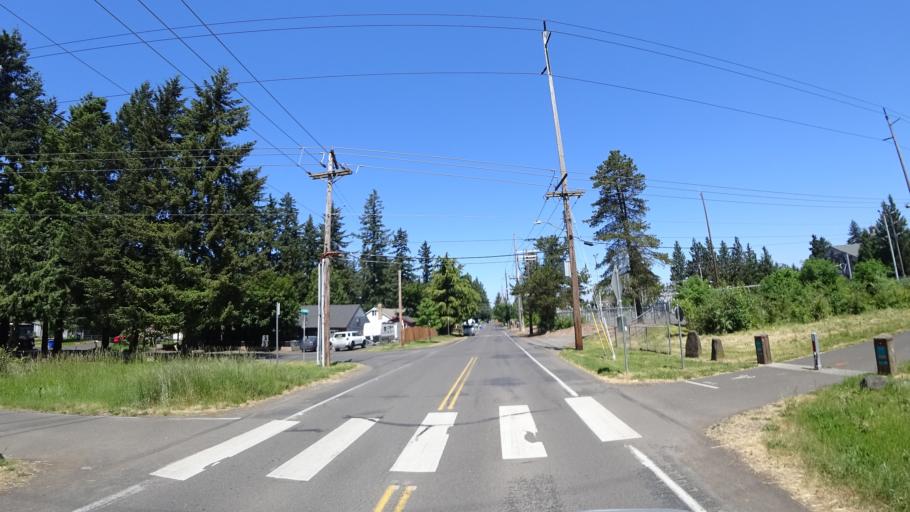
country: US
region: Oregon
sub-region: Clackamas County
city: Happy Valley
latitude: 45.4815
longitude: -122.5322
